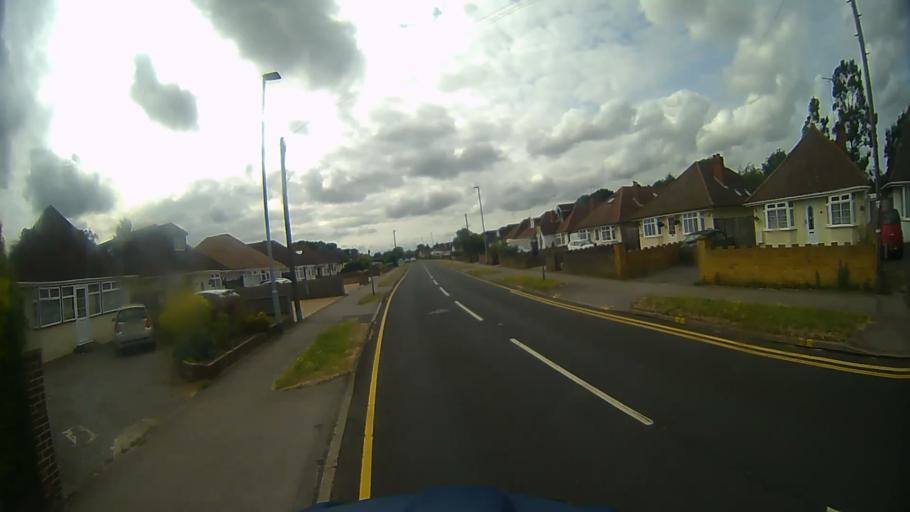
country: GB
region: England
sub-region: Wokingham
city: Earley
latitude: 51.4517
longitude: -0.9090
